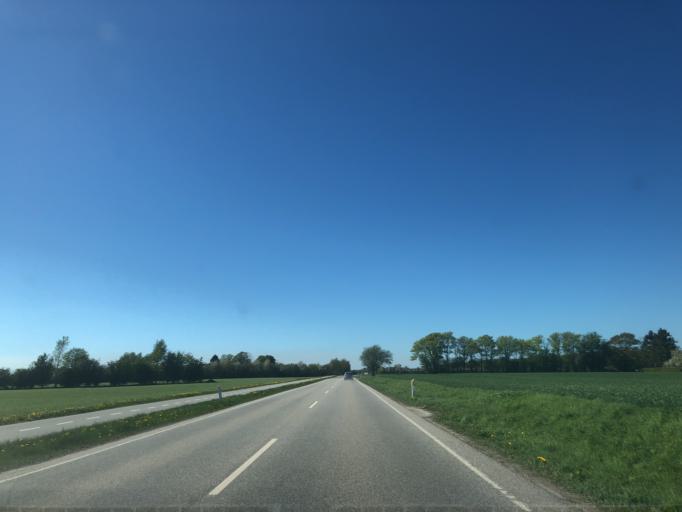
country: DK
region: Zealand
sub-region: Stevns Kommune
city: Store Heddinge
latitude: 55.3335
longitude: 12.3549
